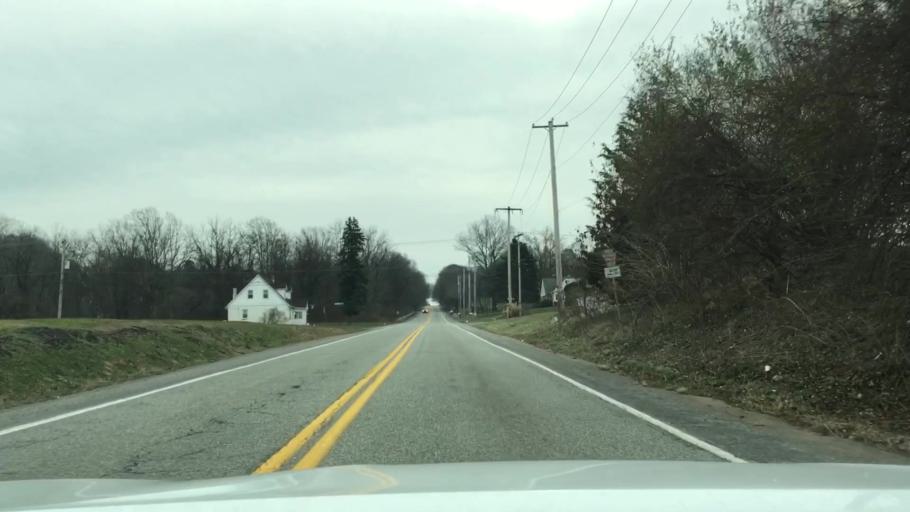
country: US
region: Pennsylvania
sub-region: Chester County
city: Spring City
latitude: 40.1931
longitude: -75.5778
